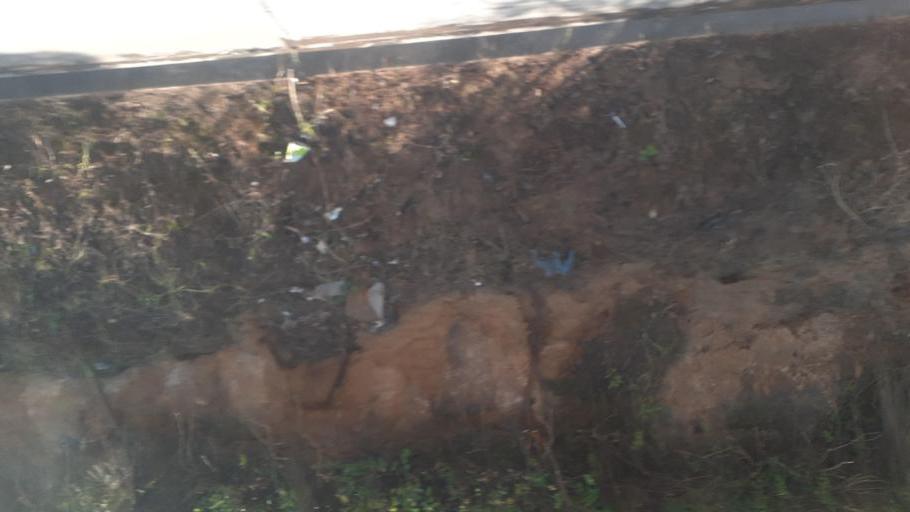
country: GT
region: Quetzaltenango
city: Cantel
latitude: 14.8142
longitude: -91.4499
